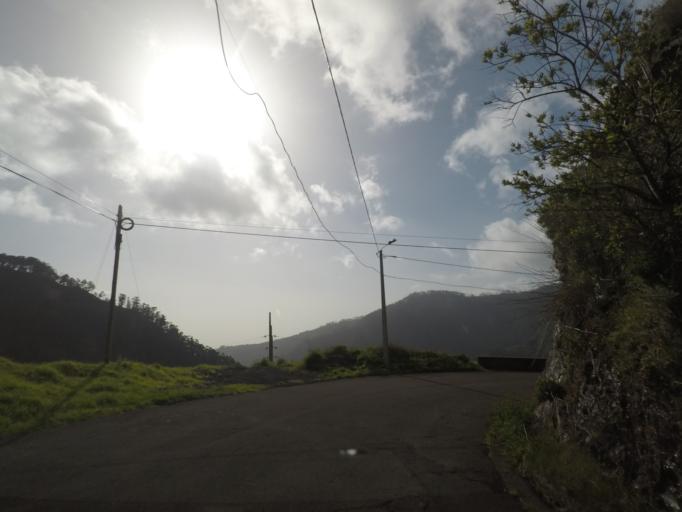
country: PT
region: Madeira
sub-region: Ribeira Brava
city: Campanario
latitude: 32.7035
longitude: -17.0281
